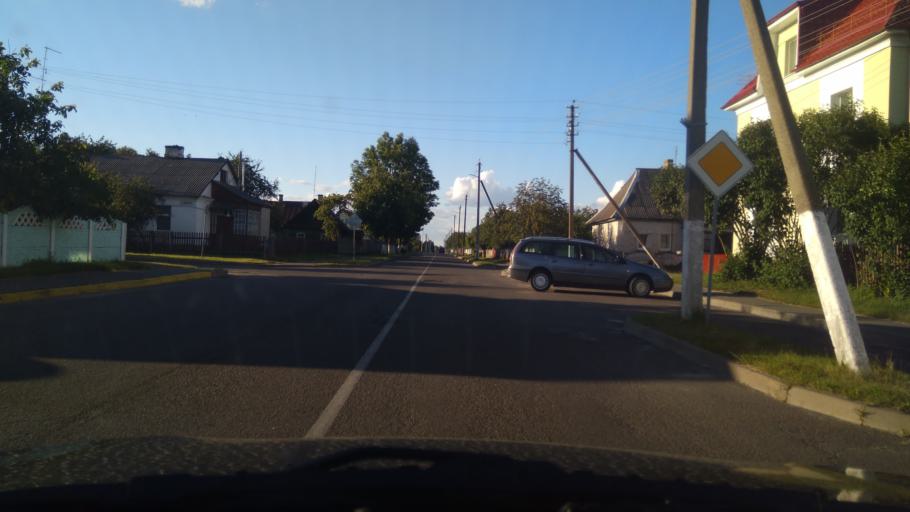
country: BY
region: Brest
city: Pruzhany
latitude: 52.5622
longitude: 24.4629
